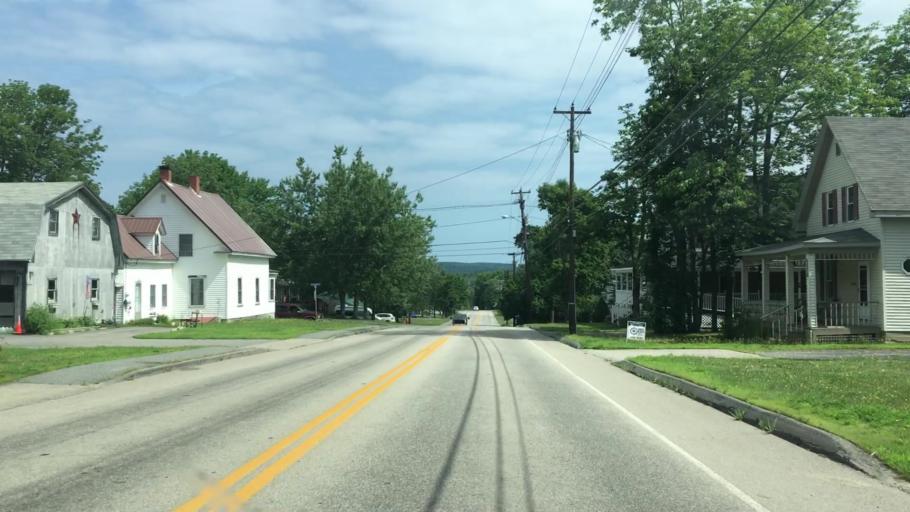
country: US
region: Maine
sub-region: Washington County
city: Calais
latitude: 45.1816
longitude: -67.2699
